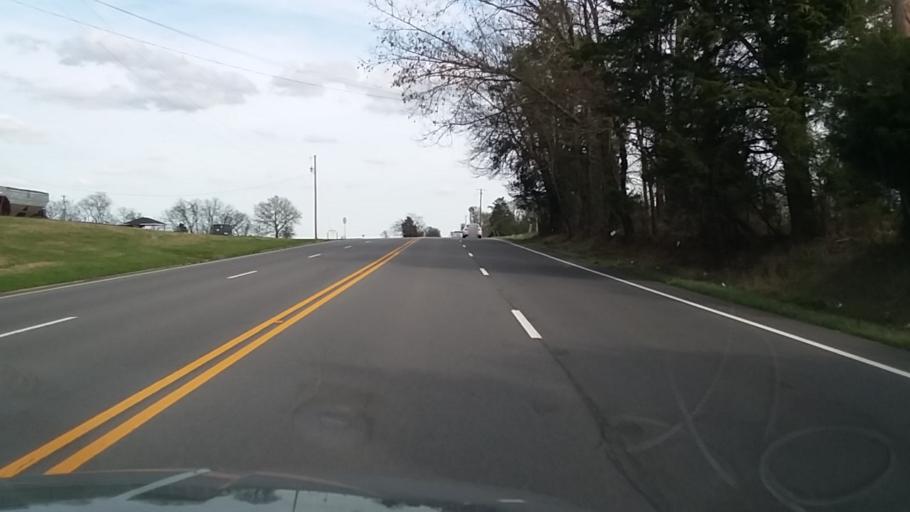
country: US
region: Alabama
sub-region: Lawrence County
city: Town Creek
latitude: 34.6820
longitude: -87.4413
